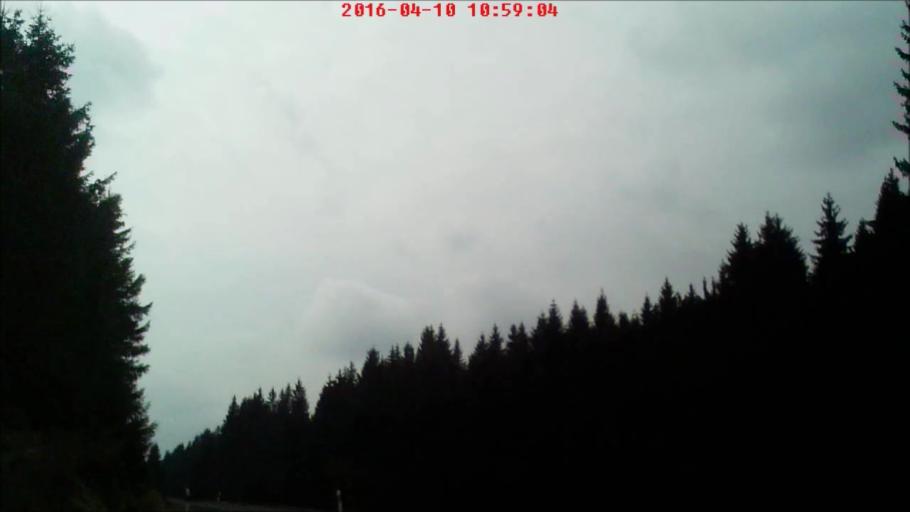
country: DE
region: Thuringia
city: Stutzerbach
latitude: 50.6121
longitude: 10.8628
